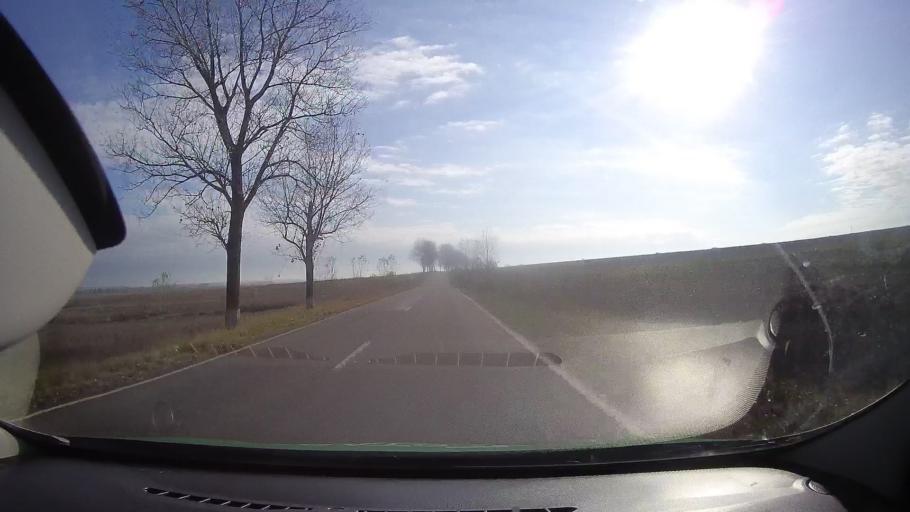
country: RO
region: Tulcea
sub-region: Comuna Mahmudia
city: Mahmudia
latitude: 45.0679
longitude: 29.1029
